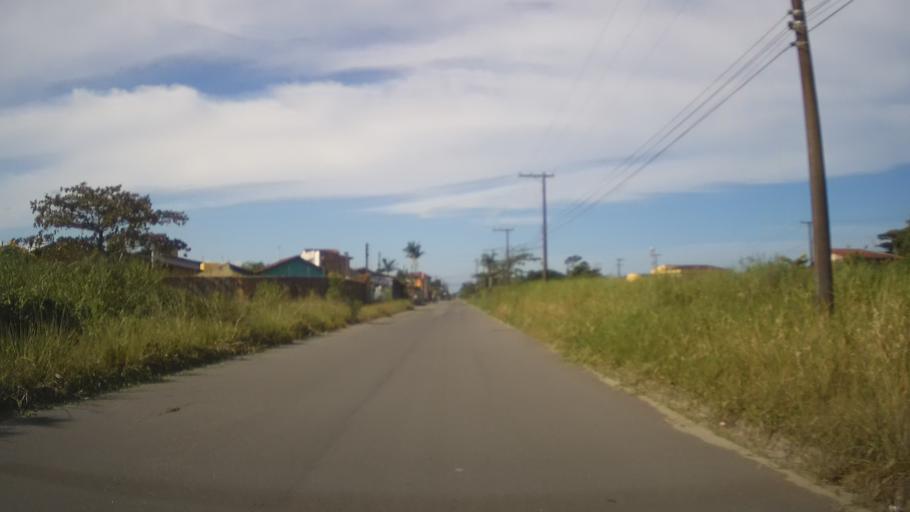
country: BR
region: Sao Paulo
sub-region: Itanhaem
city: Itanhaem
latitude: -24.2150
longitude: -46.8526
